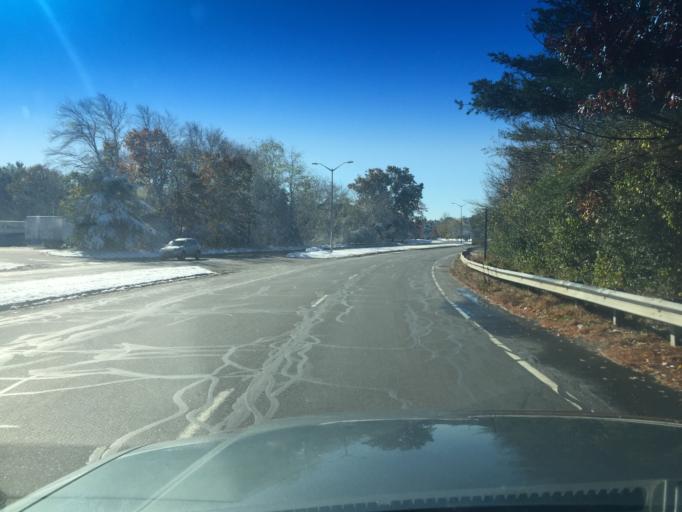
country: US
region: Massachusetts
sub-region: Bristol County
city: Norton
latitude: 41.9507
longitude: -71.1394
